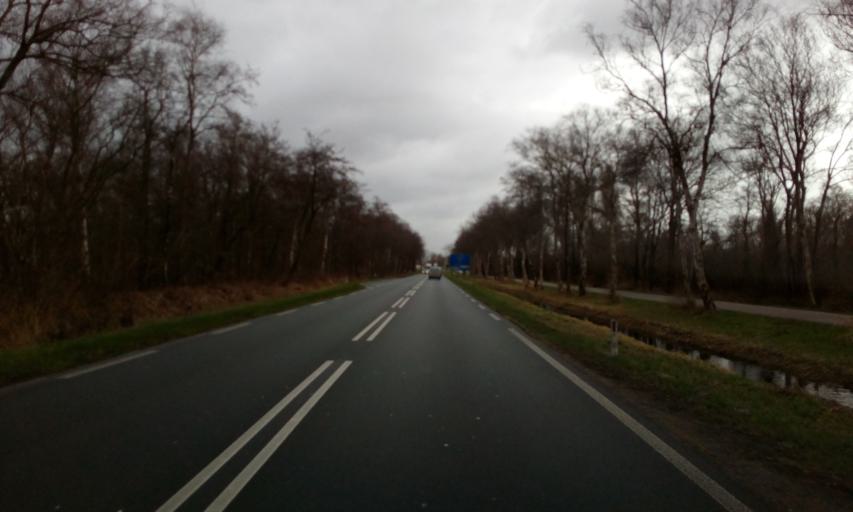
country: NL
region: North Holland
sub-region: Gemeente Wijdemeren
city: Oud-Loosdrecht
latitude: 52.2282
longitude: 5.0785
